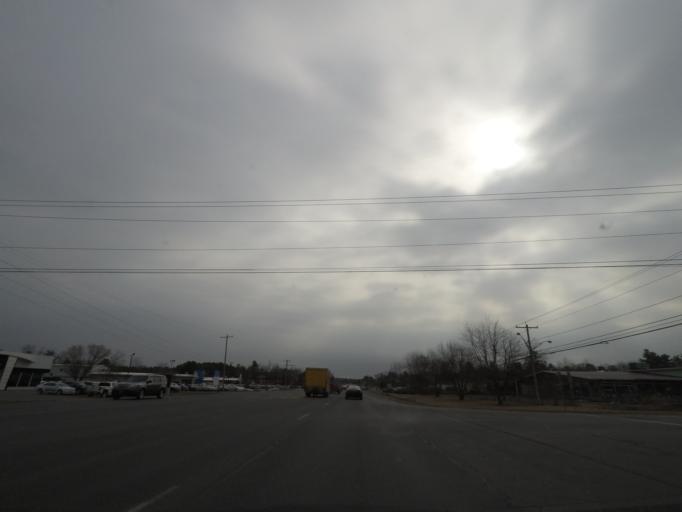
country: US
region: New York
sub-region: Warren County
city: Glens Falls
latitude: 43.3320
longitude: -73.6477
